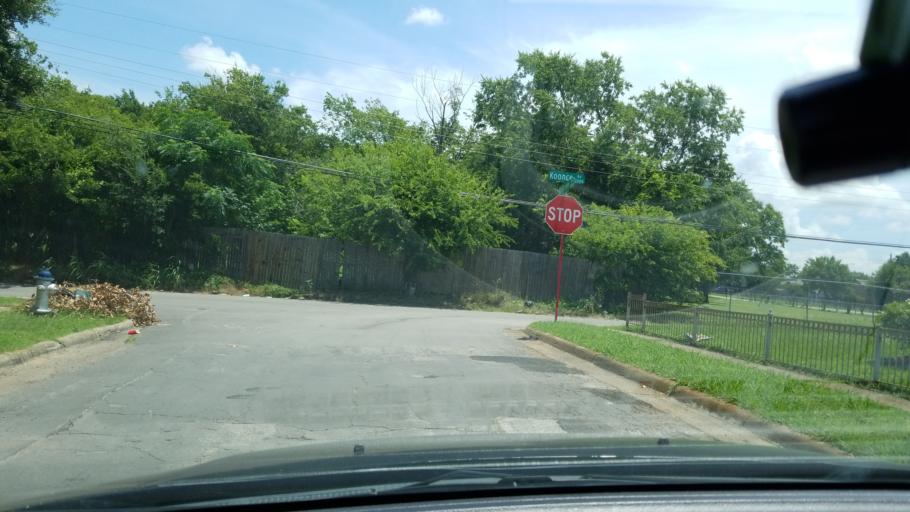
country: US
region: Texas
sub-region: Dallas County
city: Balch Springs
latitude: 32.7520
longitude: -96.6496
